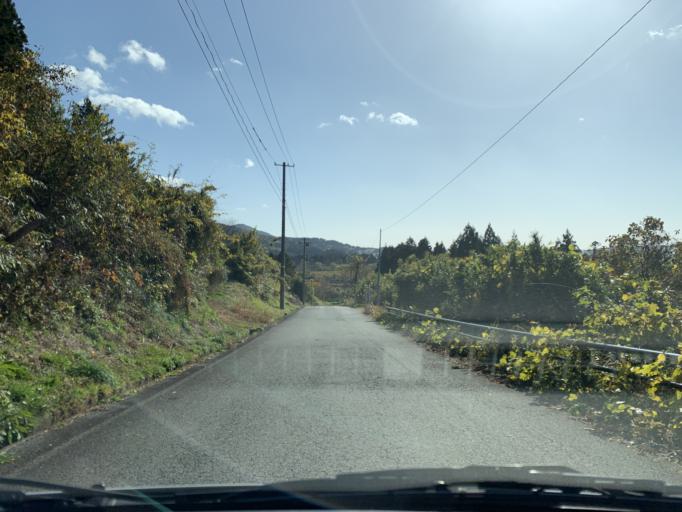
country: JP
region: Iwate
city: Ichinoseki
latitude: 39.0228
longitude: 141.1253
